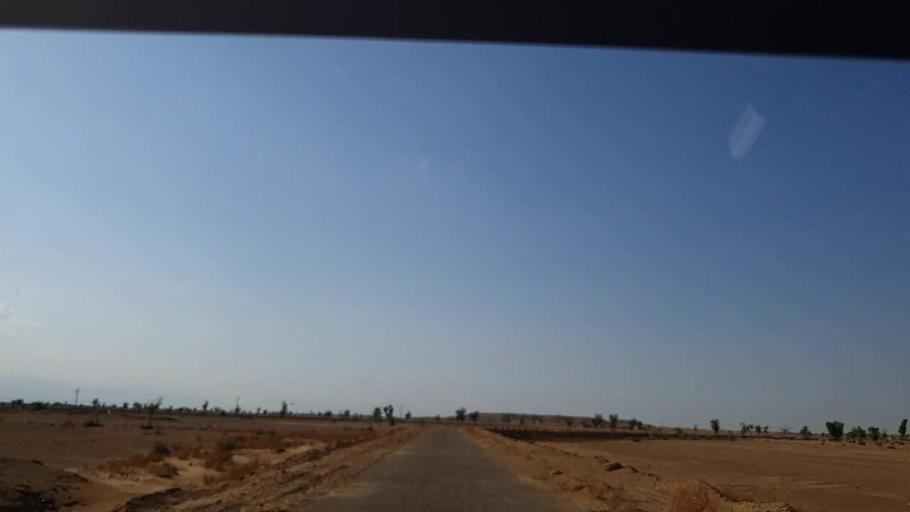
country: PK
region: Sindh
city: Johi
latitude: 26.5312
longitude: 67.5080
